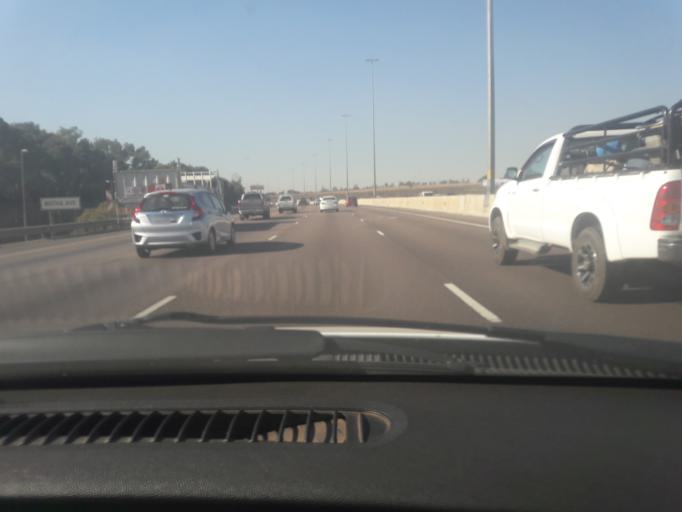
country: ZA
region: Gauteng
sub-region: City of Tshwane Metropolitan Municipality
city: Centurion
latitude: -25.8590
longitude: 28.2196
